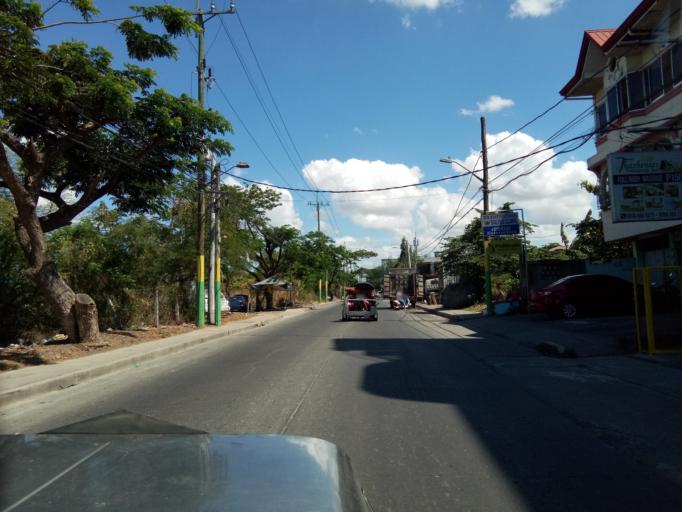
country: PH
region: Calabarzon
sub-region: Province of Cavite
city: Dasmarinas
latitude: 14.3452
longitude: 120.9465
